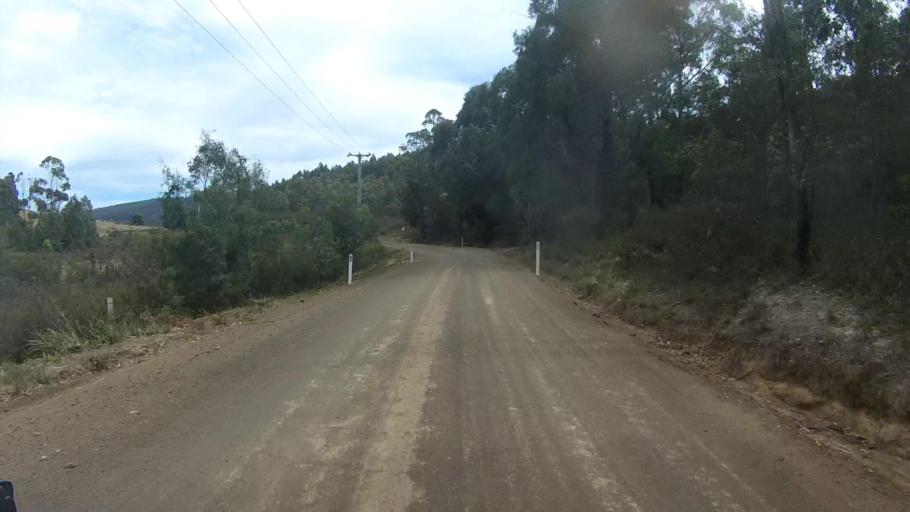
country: AU
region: Tasmania
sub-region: Sorell
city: Sorell
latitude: -42.7599
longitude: 147.8019
